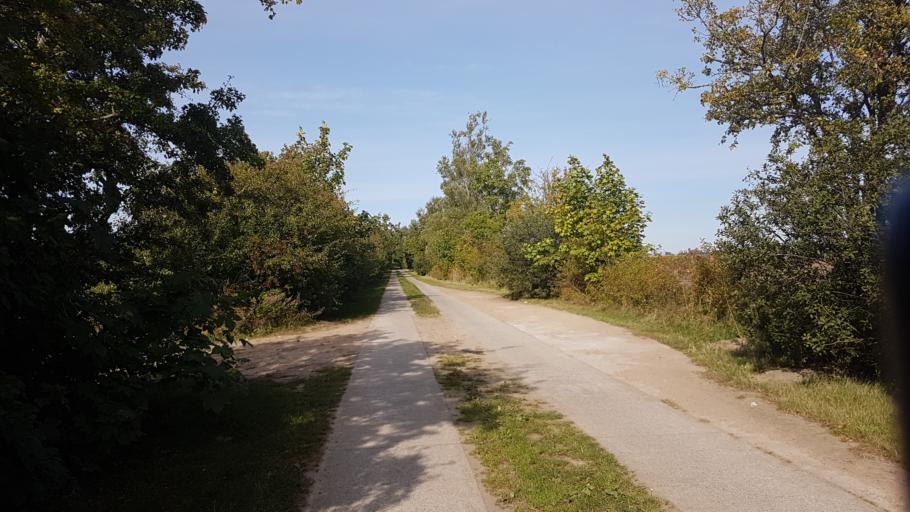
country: DE
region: Mecklenburg-Vorpommern
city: Gingst
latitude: 54.4138
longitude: 13.2573
